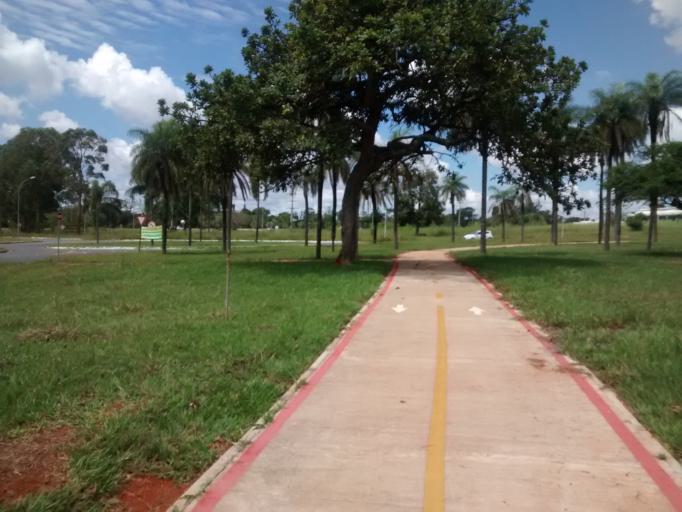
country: BR
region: Federal District
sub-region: Brasilia
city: Brasilia
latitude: -15.7630
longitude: -47.8653
